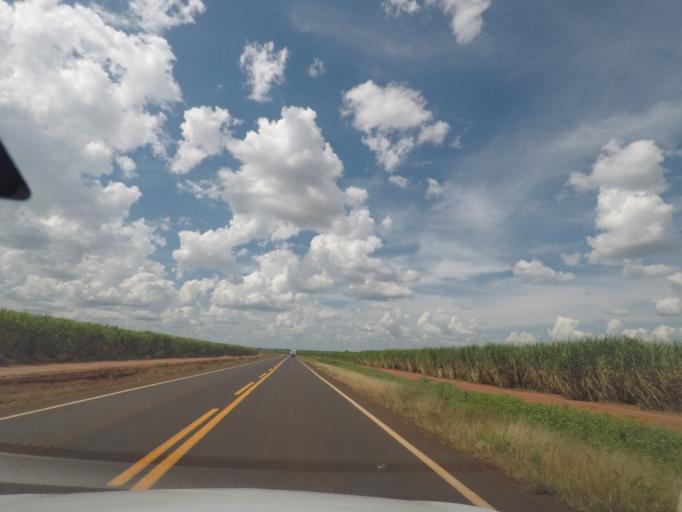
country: BR
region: Minas Gerais
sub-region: Conceicao Das Alagoas
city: Conceicao das Alagoas
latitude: -19.8415
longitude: -48.5925
